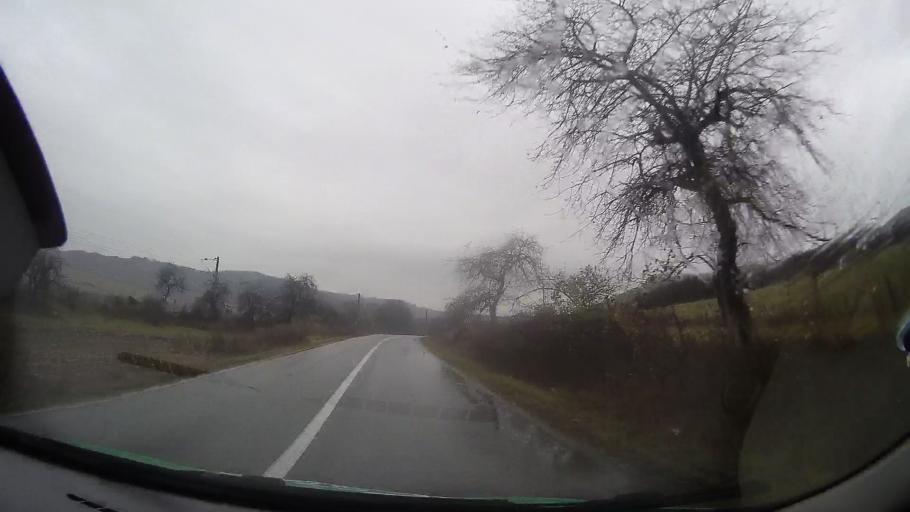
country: RO
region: Bistrita-Nasaud
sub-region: Comuna Mariselu
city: Mariselu
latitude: 47.0155
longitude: 24.5320
